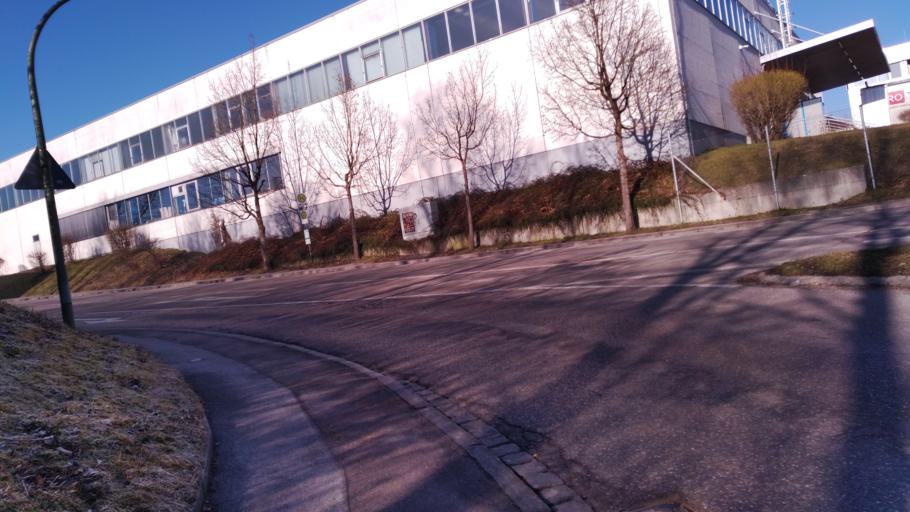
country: DE
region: Bavaria
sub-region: Upper Bavaria
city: Weilheim
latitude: 47.8493
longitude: 11.1464
